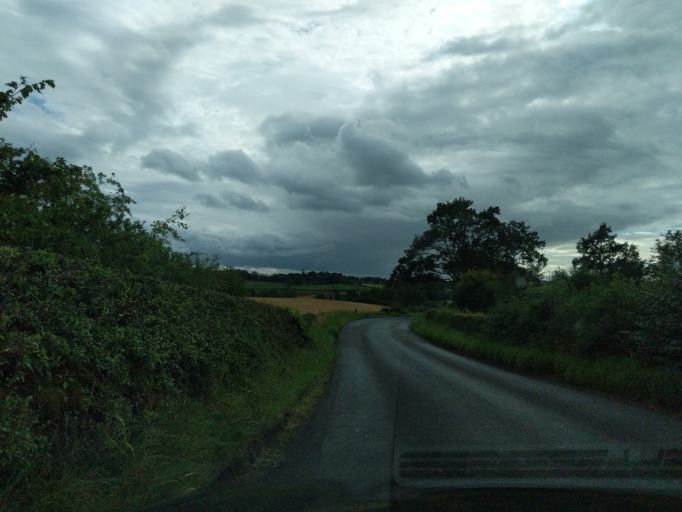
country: GB
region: Scotland
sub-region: The Scottish Borders
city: Melrose
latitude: 55.5638
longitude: -2.7160
